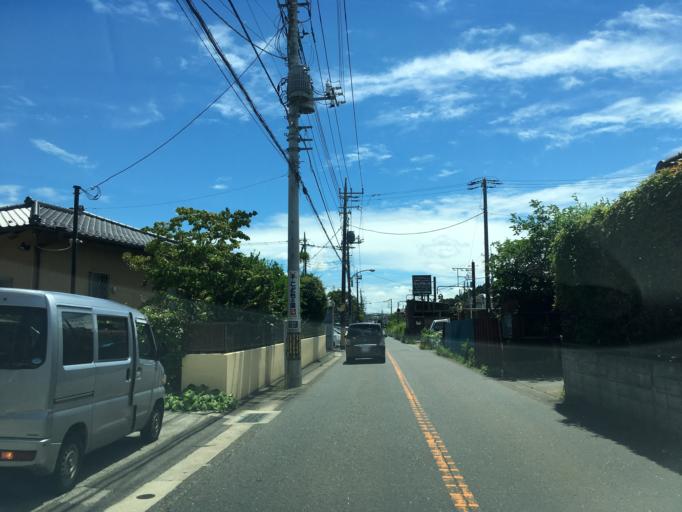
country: JP
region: Tokyo
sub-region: Machida-shi
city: Machida
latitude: 35.5533
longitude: 139.4899
